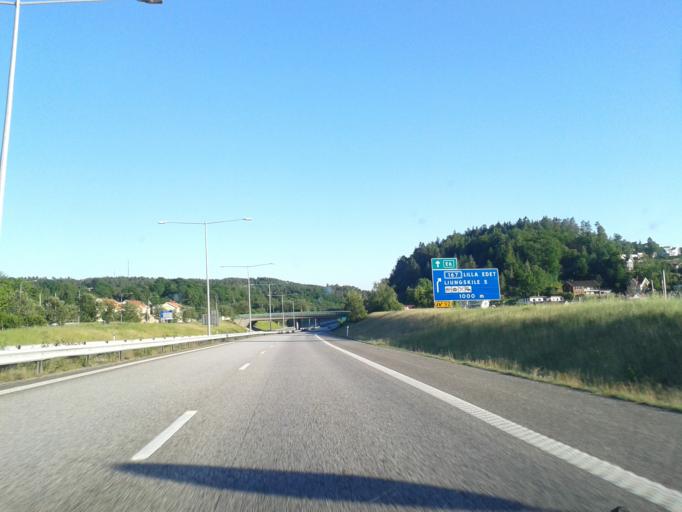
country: SE
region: Vaestra Goetaland
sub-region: Uddevalla Kommun
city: Ljungskile
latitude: 58.2244
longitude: 11.9171
